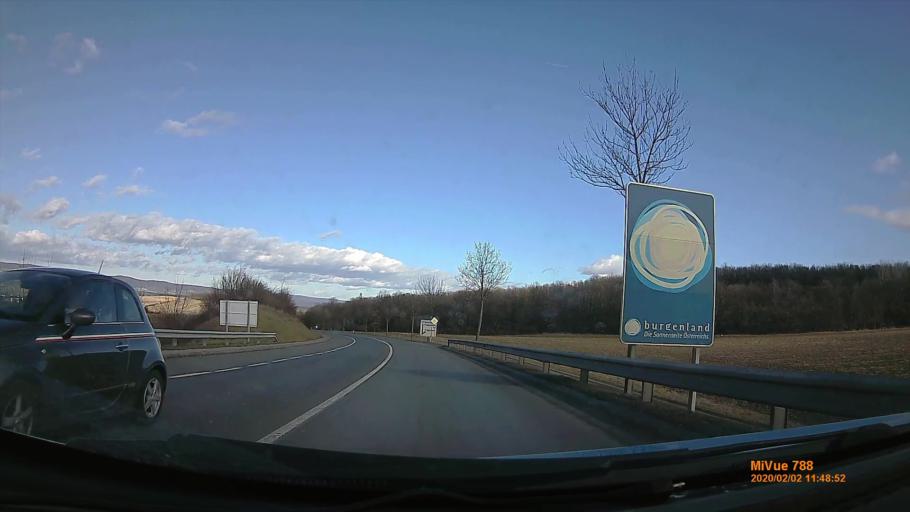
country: AT
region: Burgenland
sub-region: Eisenstadt-Umgebung
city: Klingenbach
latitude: 47.7466
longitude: 16.5446
